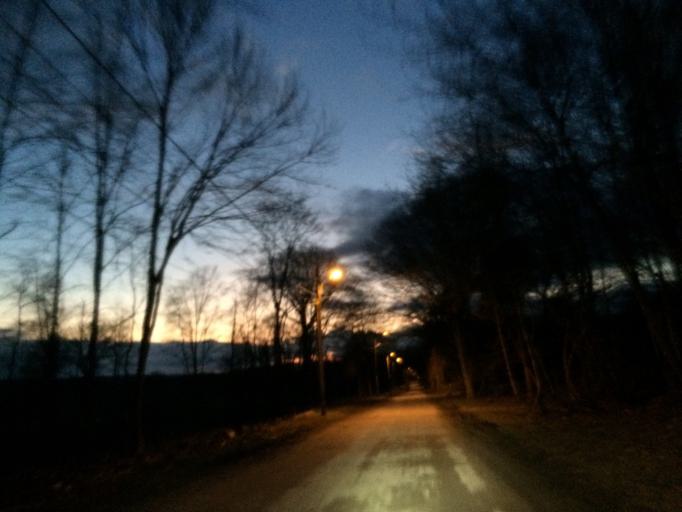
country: FR
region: Picardie
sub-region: Departement de l'Oise
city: Coye-la-Foret
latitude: 49.1528
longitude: 2.4642
